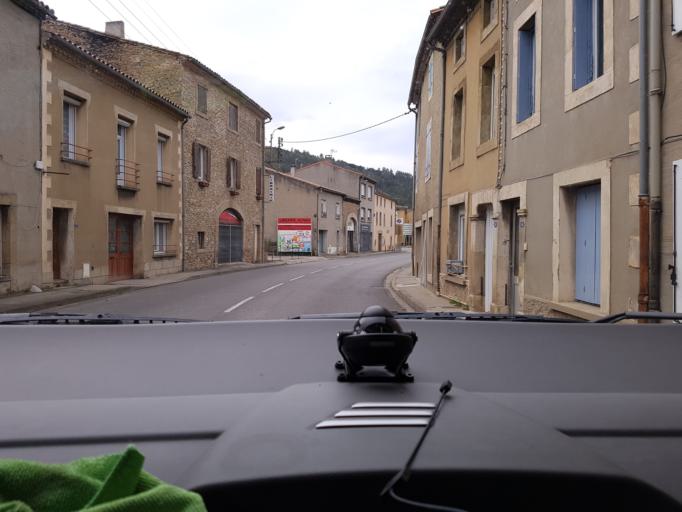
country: FR
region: Languedoc-Roussillon
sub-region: Departement de l'Aude
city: Couiza
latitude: 42.9437
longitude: 2.2563
